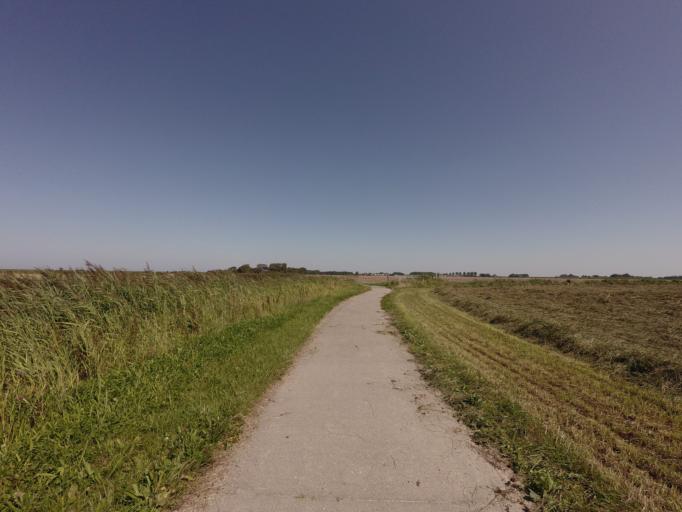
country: NL
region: Friesland
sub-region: Gemeente Dongeradeel
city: Anjum
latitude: 53.3937
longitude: 6.0696
